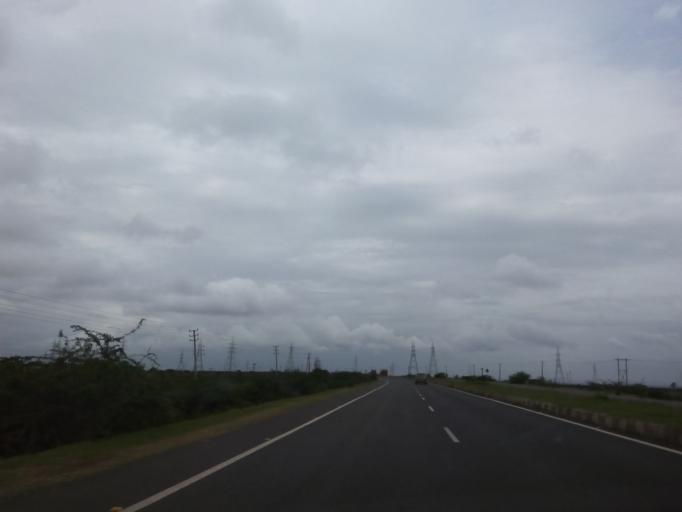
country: IN
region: Karnataka
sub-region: Haveri
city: Ranibennur
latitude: 14.6129
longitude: 75.6094
